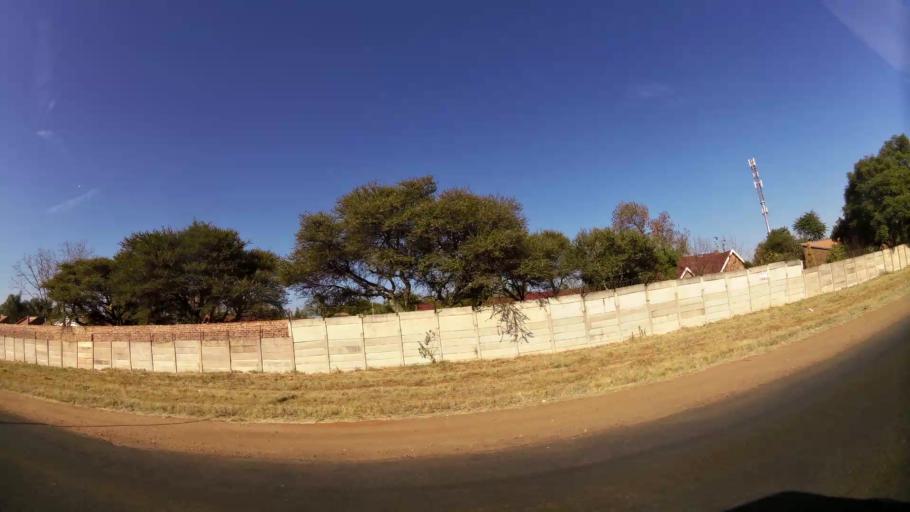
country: ZA
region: Gauteng
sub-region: City of Tshwane Metropolitan Municipality
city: Pretoria
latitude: -25.6544
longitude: 28.1401
